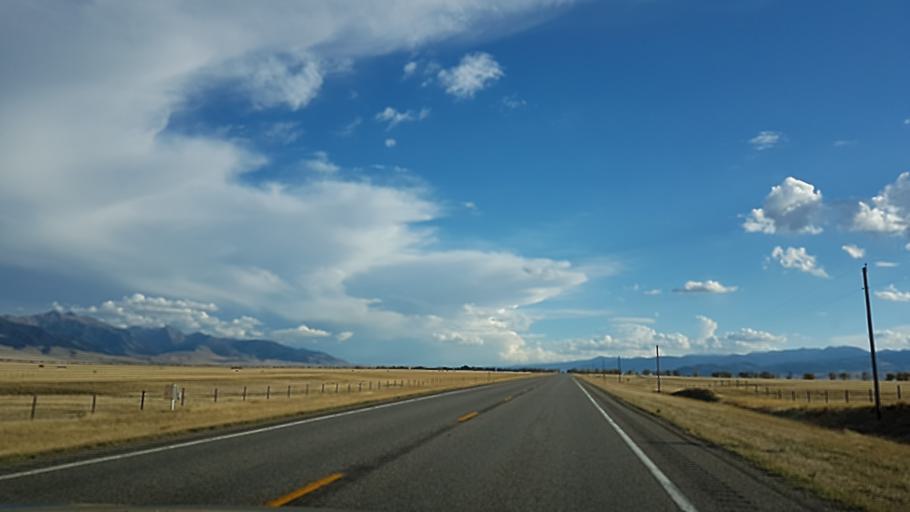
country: US
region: Montana
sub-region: Madison County
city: Virginia City
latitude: 45.2270
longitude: -111.6789
